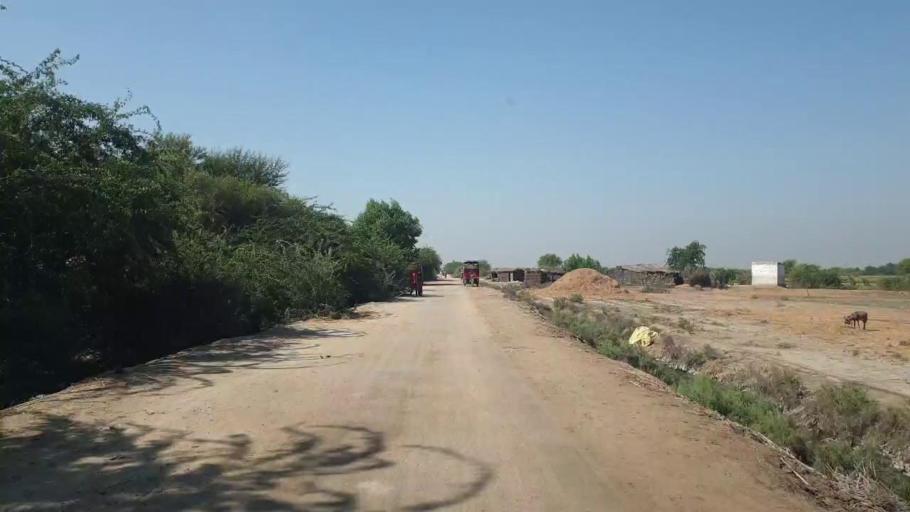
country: PK
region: Sindh
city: Talhar
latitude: 24.8283
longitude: 68.7728
